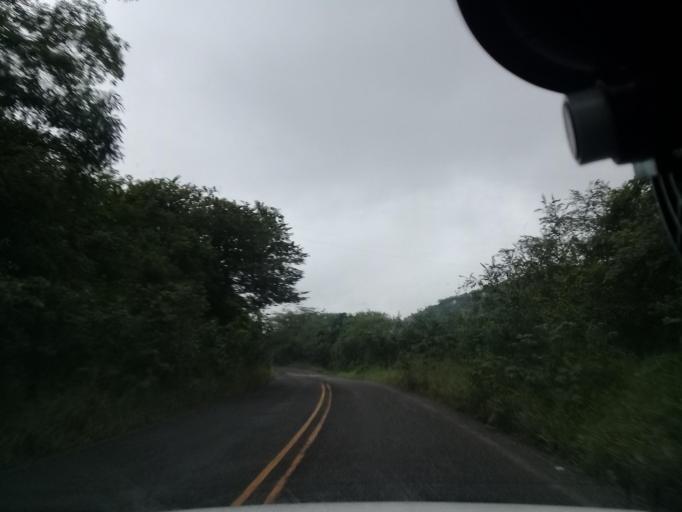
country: MX
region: Veracruz
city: Platon Sanchez
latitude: 21.2327
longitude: -98.3681
